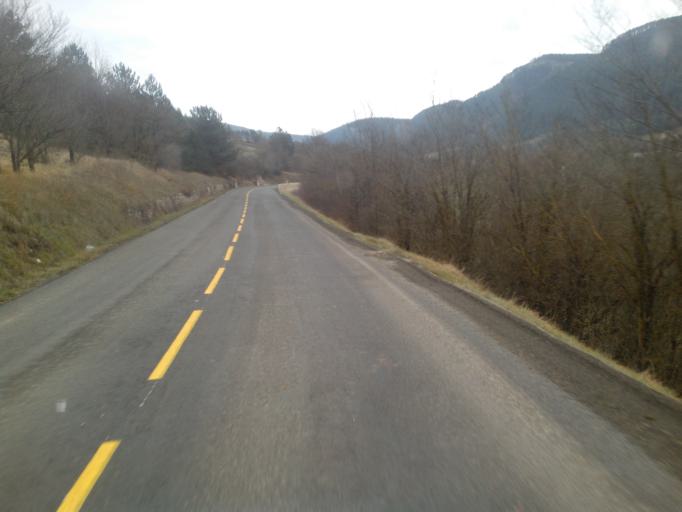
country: FR
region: Languedoc-Roussillon
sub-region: Departement de la Lozere
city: Mende
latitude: 44.4590
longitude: 3.5227
